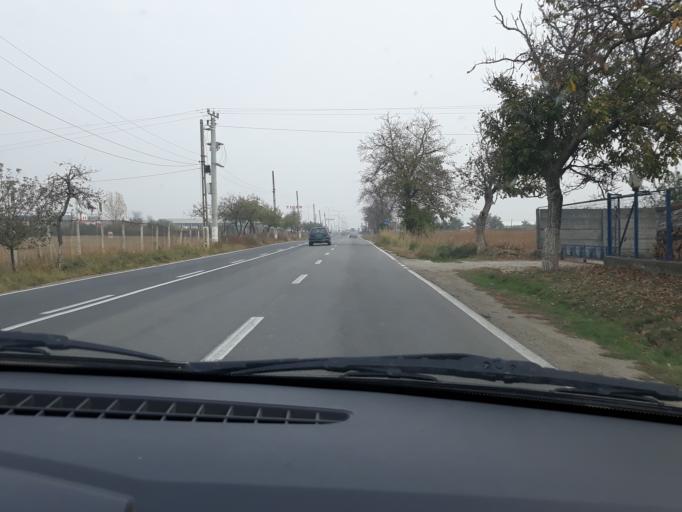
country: RO
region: Bihor
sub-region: Comuna Santandrei
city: Santandrei
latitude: 47.0508
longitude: 21.8816
